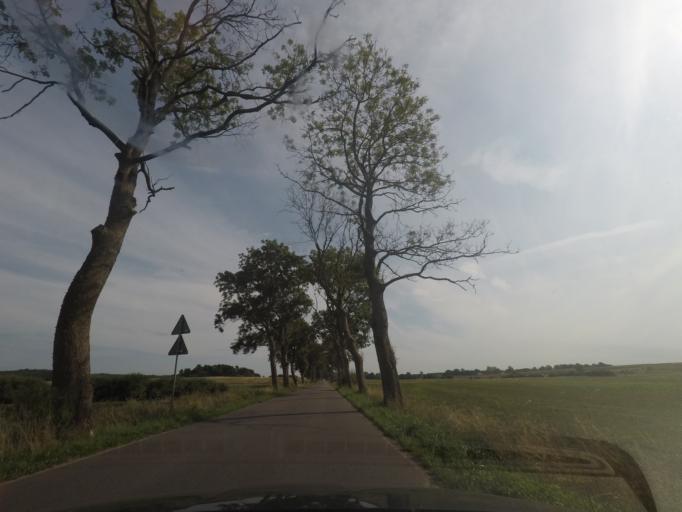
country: PL
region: Pomeranian Voivodeship
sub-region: Powiat slupski
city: Smoldzino
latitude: 54.6421
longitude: 17.2626
